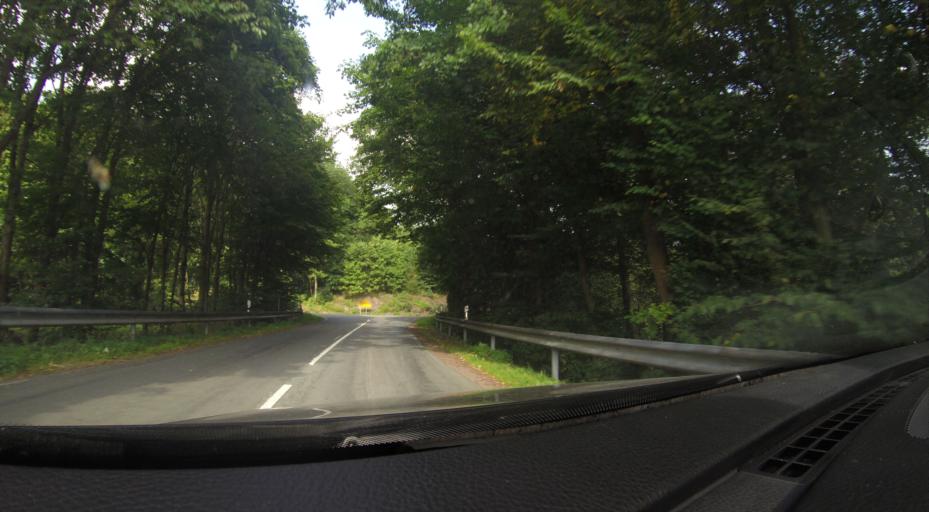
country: DE
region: North Rhine-Westphalia
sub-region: Regierungsbezirk Arnsberg
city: Medebach
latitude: 51.2075
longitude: 8.6744
